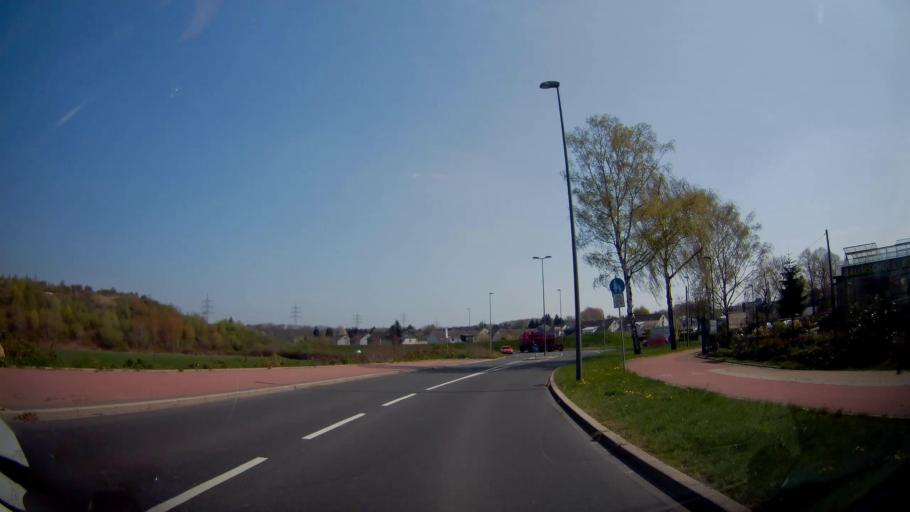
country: DE
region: North Rhine-Westphalia
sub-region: Regierungsbezirk Munster
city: Gelsenkirchen
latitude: 51.5012
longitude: 7.1444
